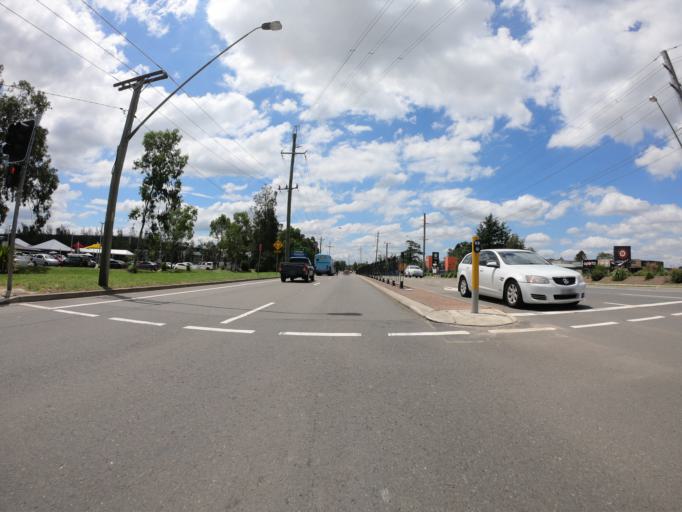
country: AU
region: New South Wales
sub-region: Penrith Municipality
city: Penrith
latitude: -33.7455
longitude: 150.6910
